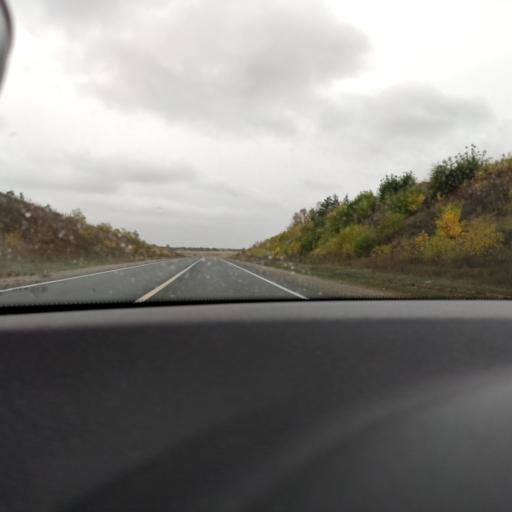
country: RU
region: Samara
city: Mirnyy
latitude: 53.5979
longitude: 50.2768
